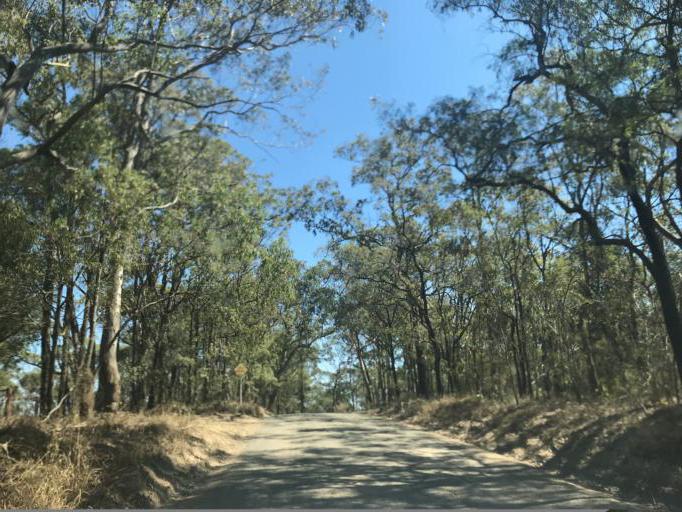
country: AU
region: New South Wales
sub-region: Hawkesbury
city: Pitt Town
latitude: -33.4641
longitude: 150.8443
